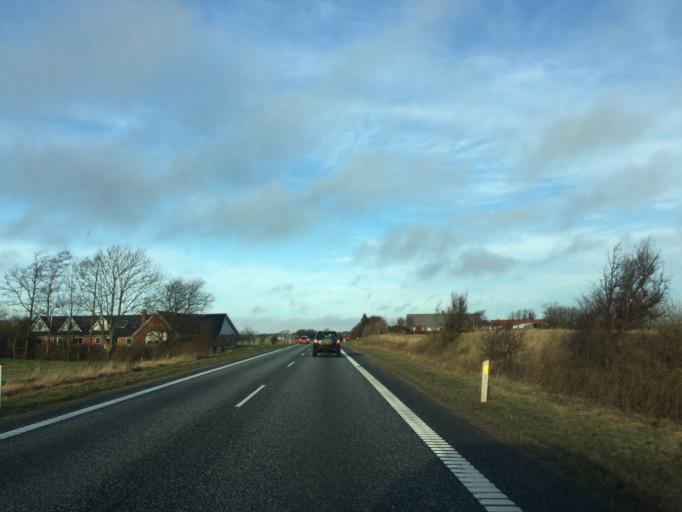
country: DK
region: North Denmark
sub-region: Thisted Kommune
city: Thisted
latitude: 56.8950
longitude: 8.5986
